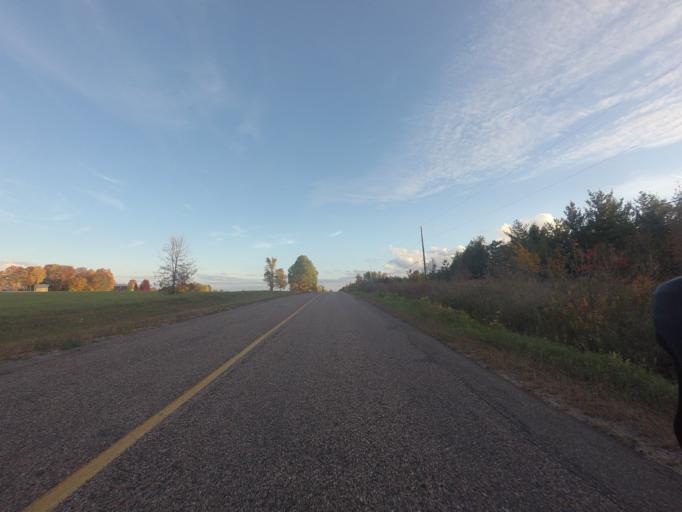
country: CA
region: Ontario
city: Renfrew
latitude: 45.4622
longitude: -76.9764
